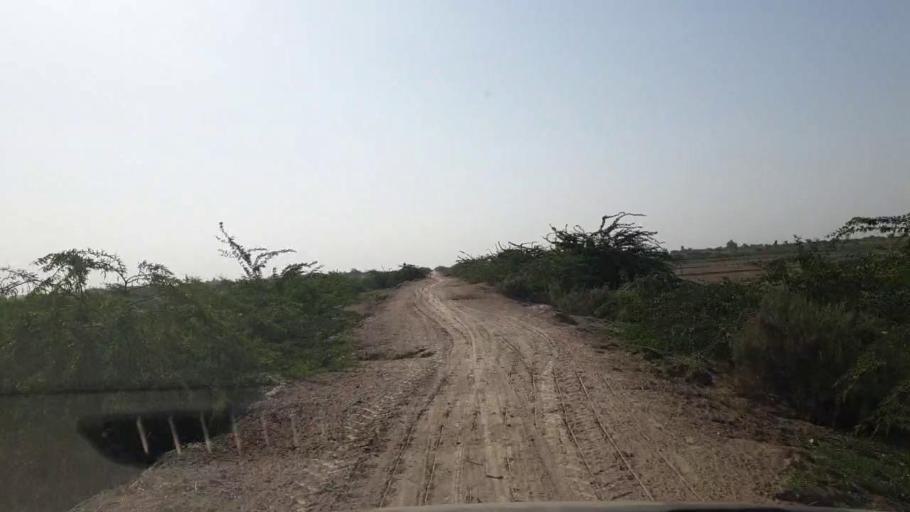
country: PK
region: Sindh
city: Kadhan
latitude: 24.5826
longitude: 69.0791
